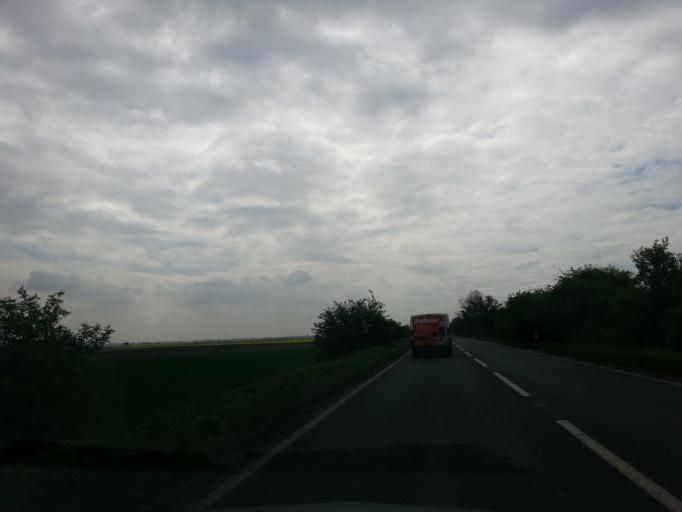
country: GB
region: England
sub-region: Cambridgeshire
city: Wisbech
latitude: 52.6277
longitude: 0.0965
